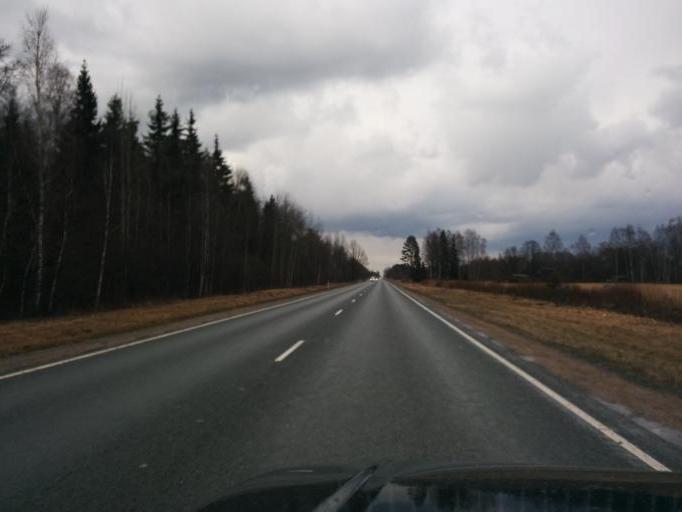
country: LV
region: Ozolnieku
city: Ozolnieki
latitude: 56.7183
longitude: 23.8403
